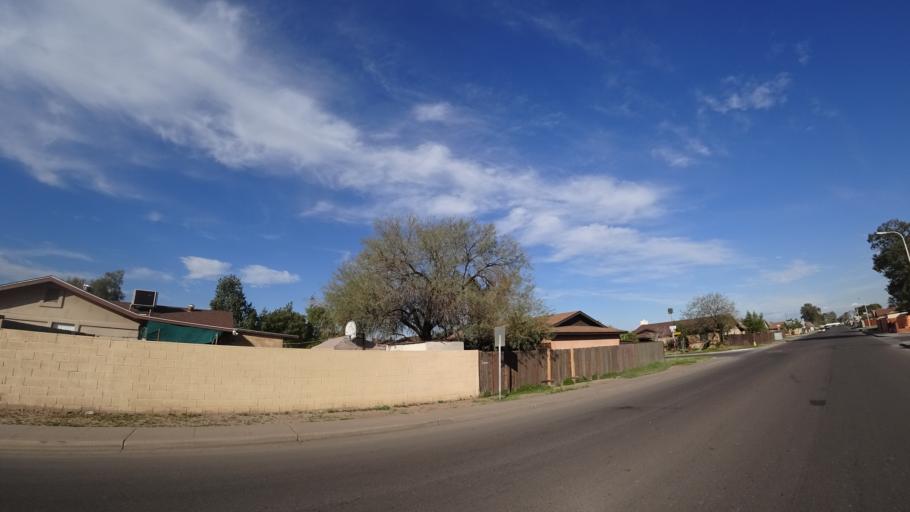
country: US
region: Arizona
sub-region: Maricopa County
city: Tolleson
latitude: 33.4588
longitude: -112.1916
